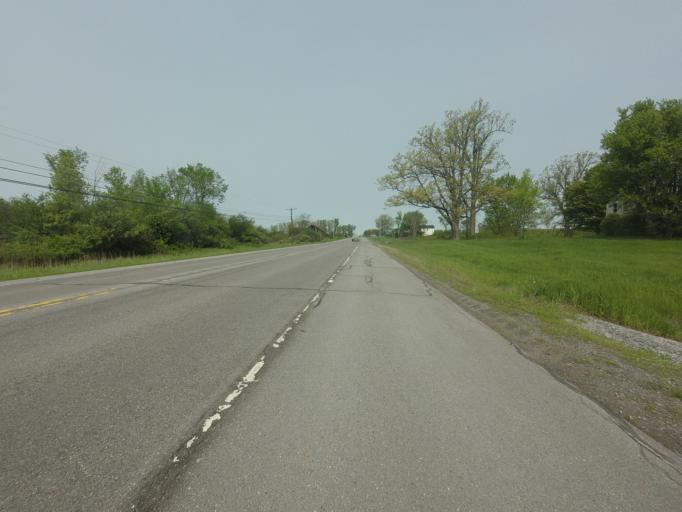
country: US
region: New York
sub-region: Jefferson County
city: Dexter
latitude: 44.0349
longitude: -76.0624
